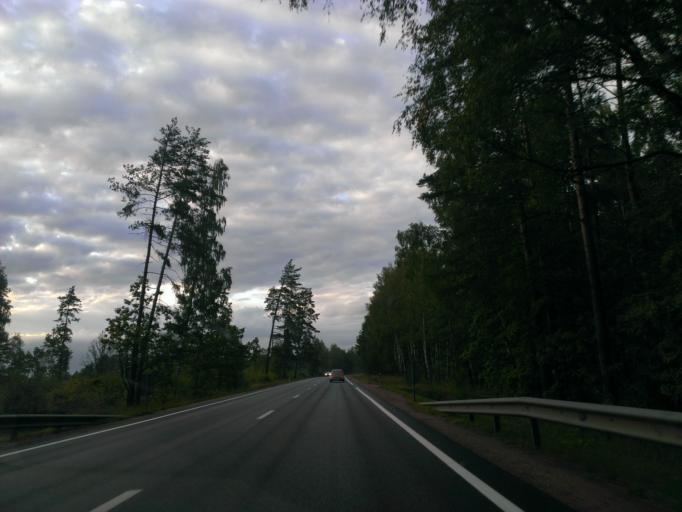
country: LV
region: Riga
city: Bergi
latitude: 56.9484
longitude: 24.3796
